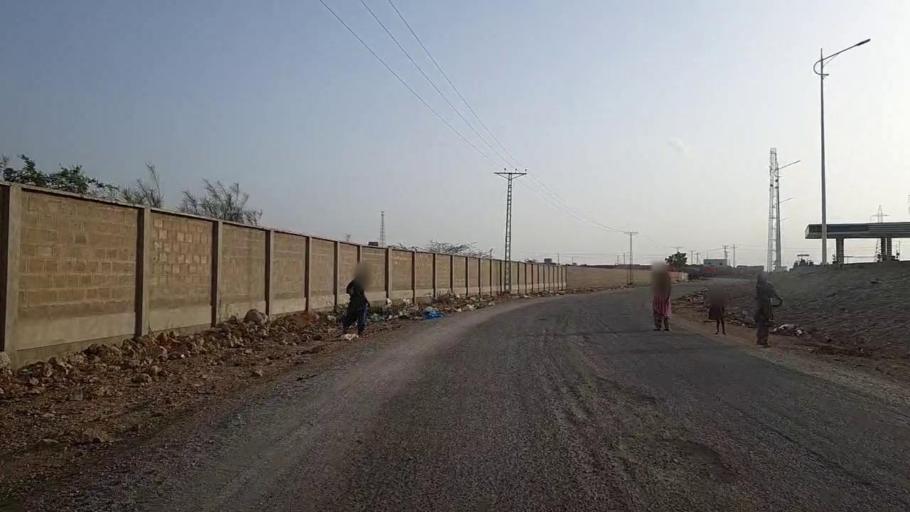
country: PK
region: Sindh
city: Thatta
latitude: 25.1761
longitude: 67.8025
